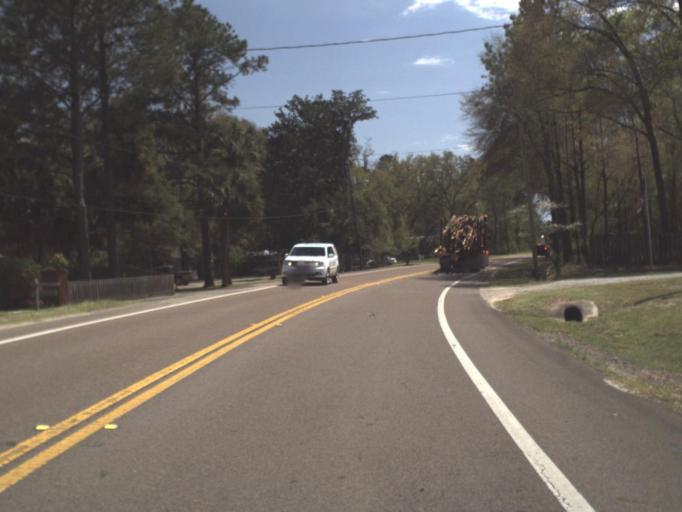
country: US
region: Florida
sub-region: Walton County
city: DeFuniak Springs
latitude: 30.7203
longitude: -85.9361
